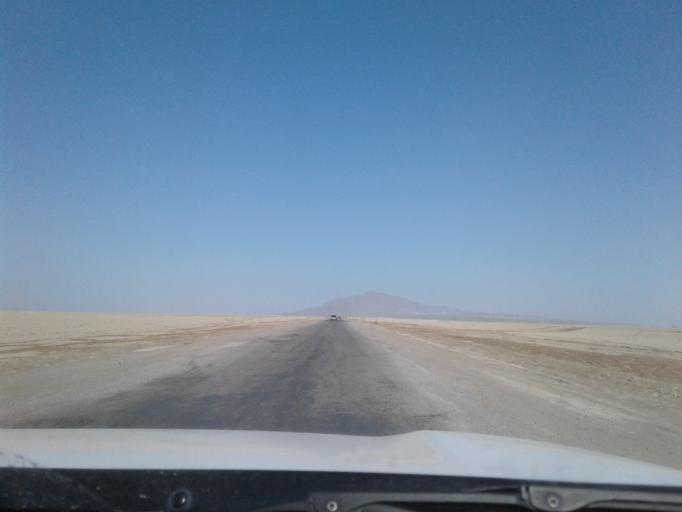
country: TM
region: Balkan
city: Gumdag
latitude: 39.2132
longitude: 54.6395
